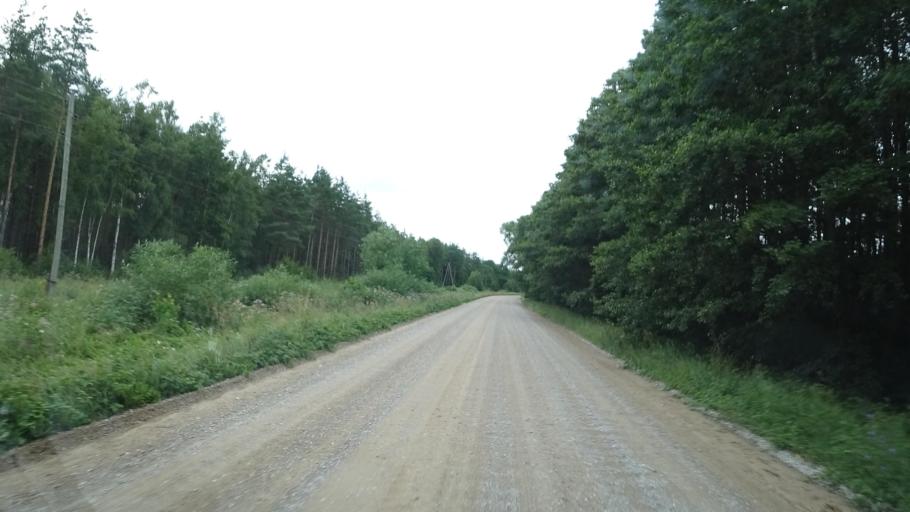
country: LV
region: Liepaja
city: Vec-Liepaja
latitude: 56.6189
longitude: 21.0413
